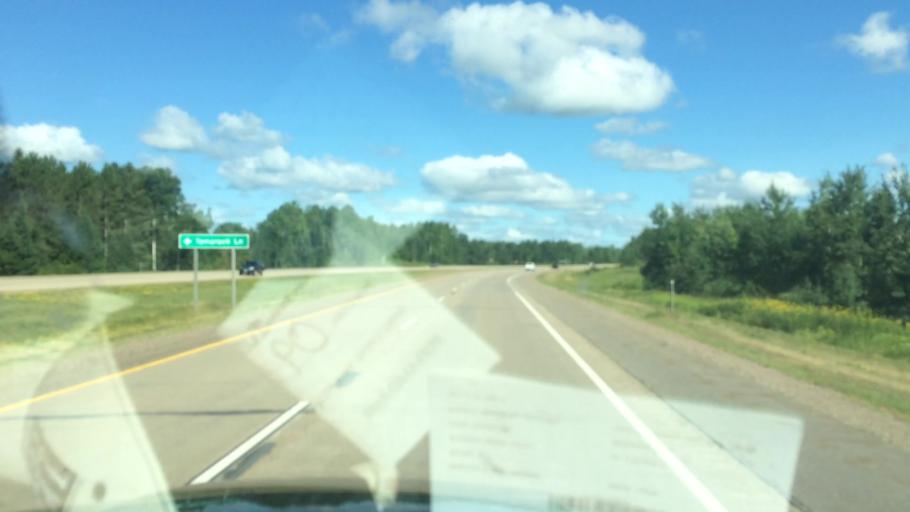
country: US
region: Wisconsin
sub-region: Lincoln County
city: Tomahawk
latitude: 45.3790
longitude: -89.6695
